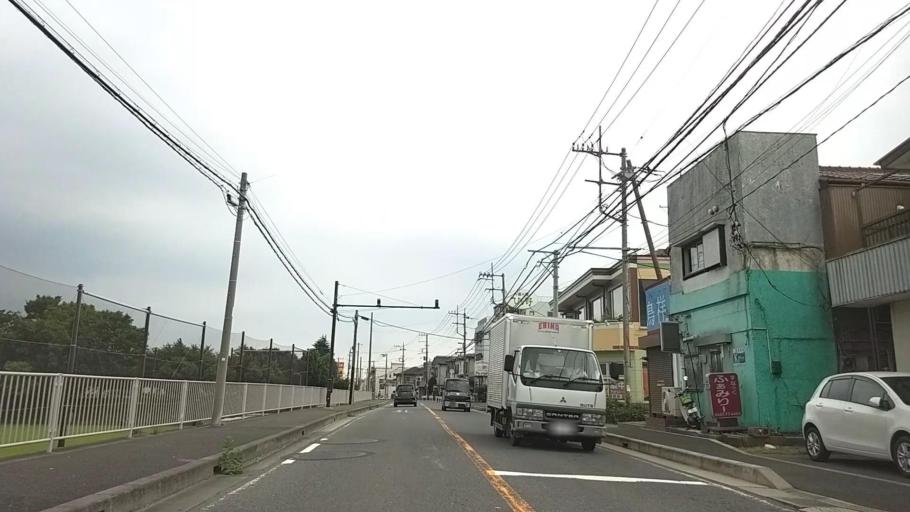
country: JP
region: Kanagawa
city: Minami-rinkan
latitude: 35.4615
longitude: 139.4244
